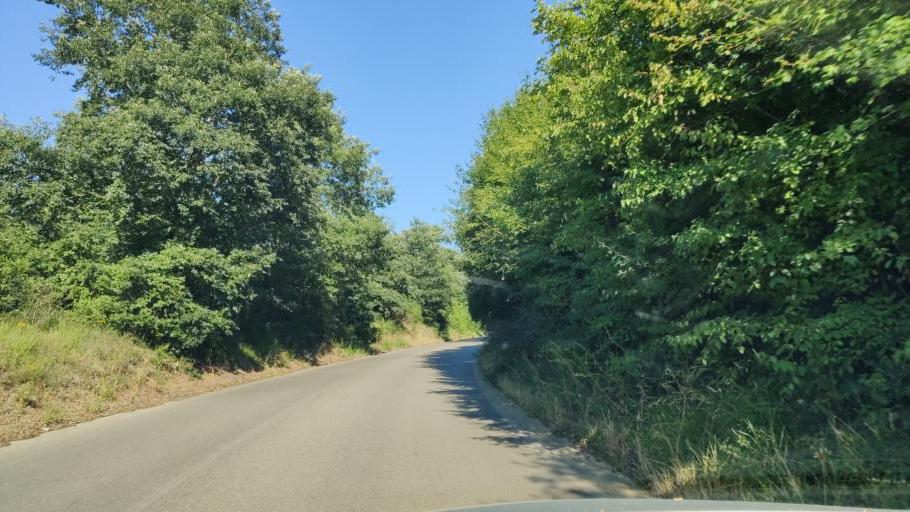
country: IT
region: Umbria
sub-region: Provincia di Terni
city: Penna in Teverina
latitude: 42.4789
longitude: 12.3680
